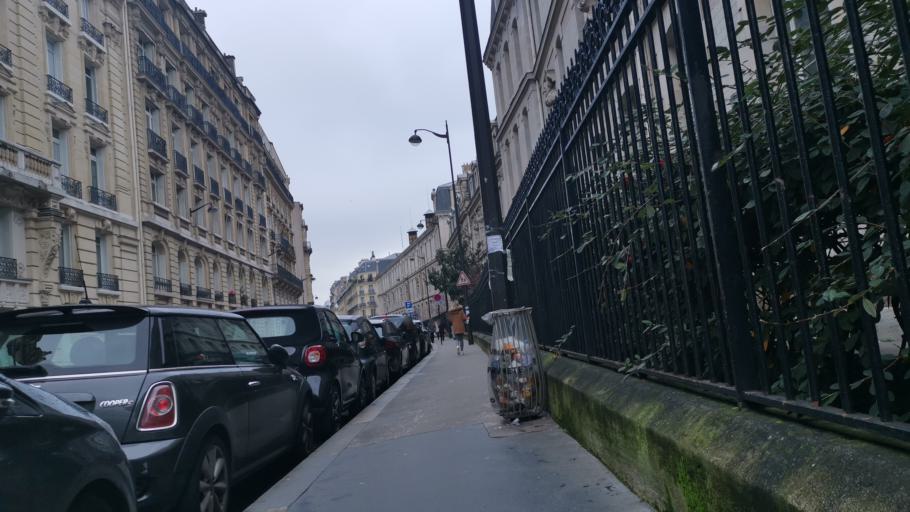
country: FR
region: Ile-de-France
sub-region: Departement des Hauts-de-Seine
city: Neuilly-sur-Seine
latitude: 48.8651
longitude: 2.2787
